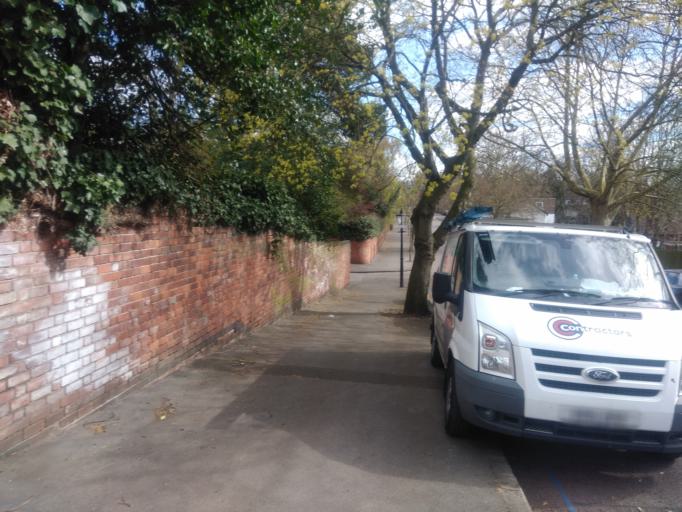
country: GB
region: England
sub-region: Nottingham
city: Nottingham
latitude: 52.9479
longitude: -1.1657
